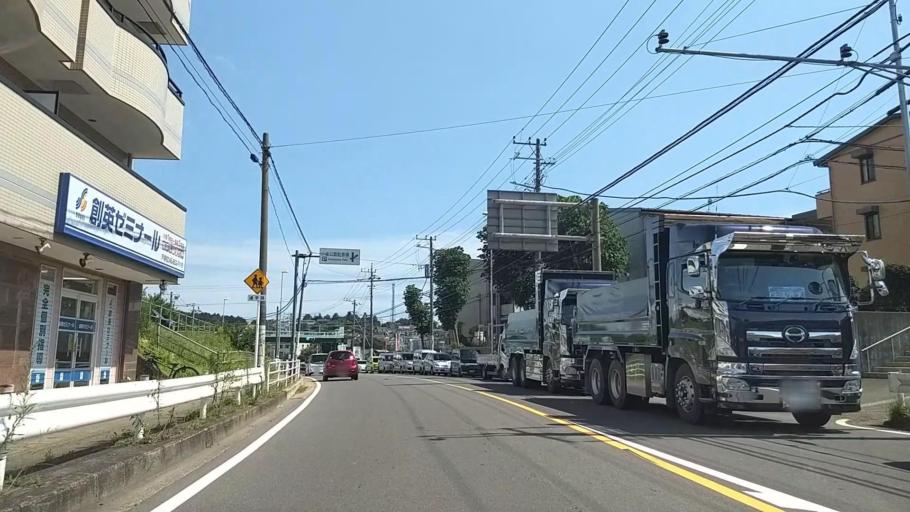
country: JP
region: Kanagawa
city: Fujisawa
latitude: 35.3759
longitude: 139.5063
